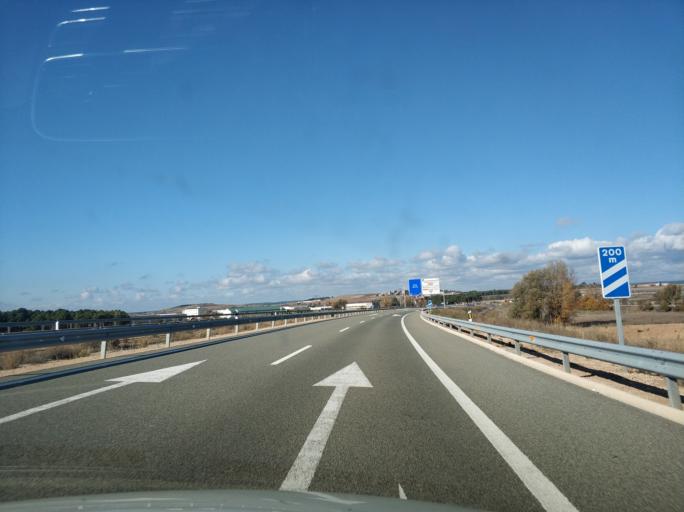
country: ES
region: Castille and Leon
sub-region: Provincia de Soria
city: Almazan
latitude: 41.4641
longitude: -2.5227
